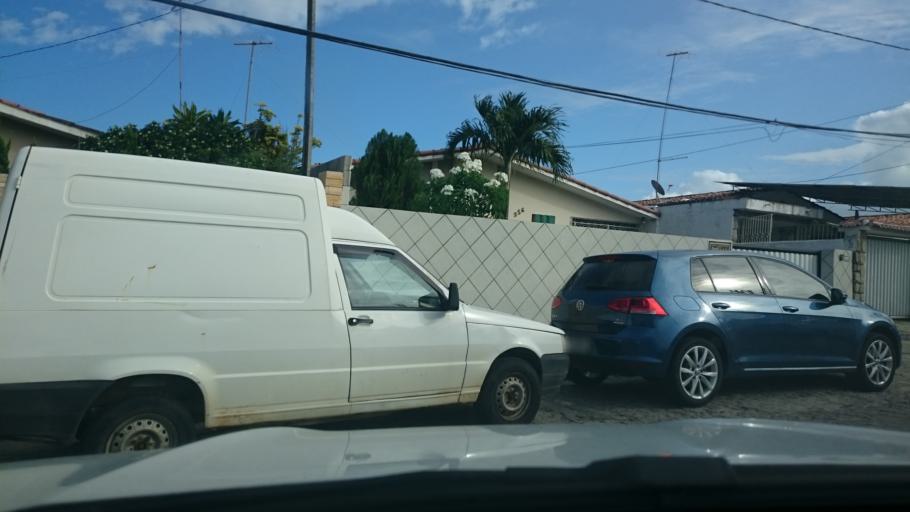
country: BR
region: Paraiba
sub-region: Joao Pessoa
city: Joao Pessoa
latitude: -7.1498
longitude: -34.8422
